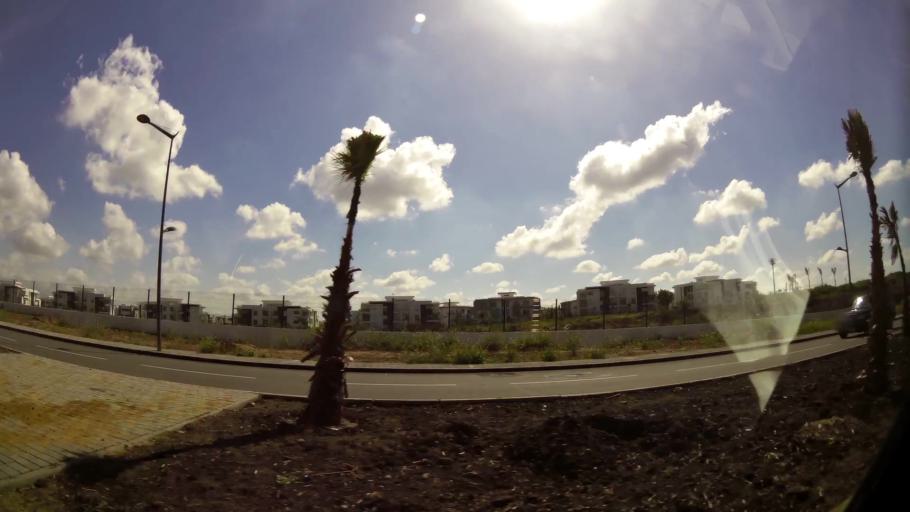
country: MA
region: Grand Casablanca
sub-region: Nouaceur
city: Bouskoura
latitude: 33.4760
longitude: -7.6030
